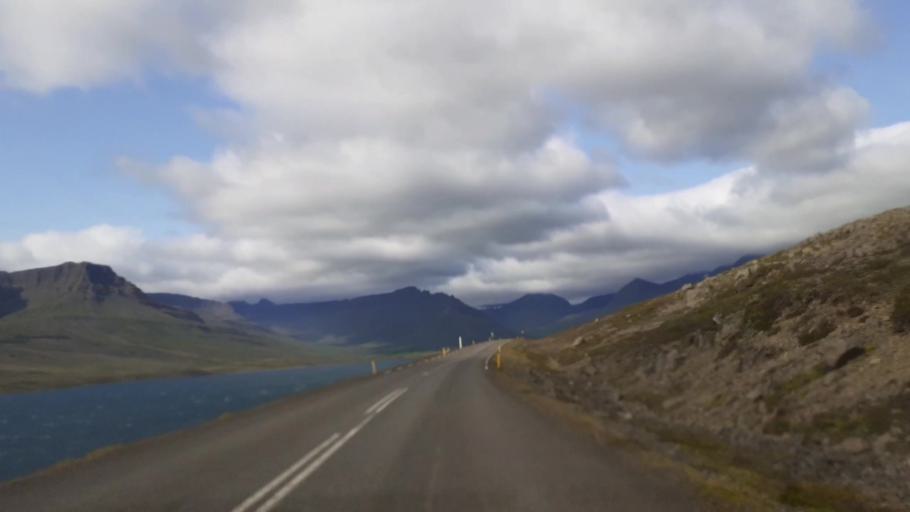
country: IS
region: East
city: Eskifjoerdur
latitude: 64.9225
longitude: -13.9726
